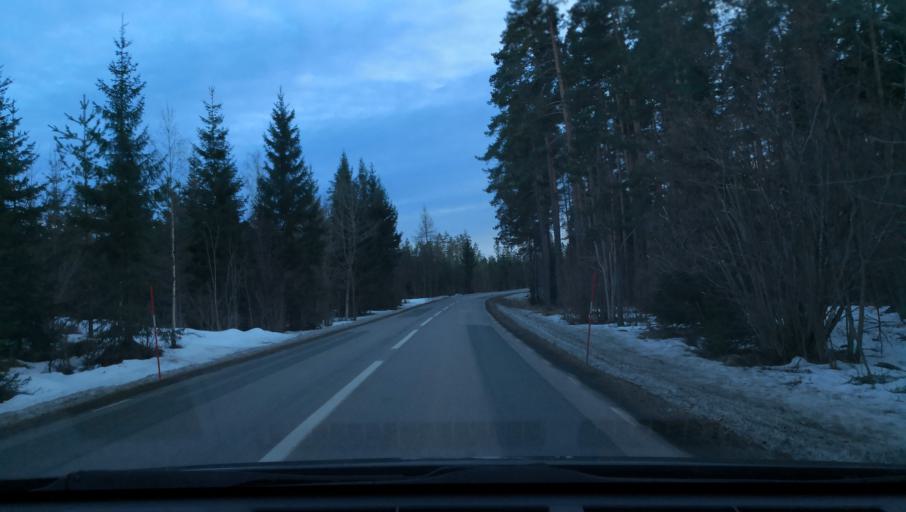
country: SE
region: Uppsala
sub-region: Osthammars Kommun
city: Osterbybruk
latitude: 60.2611
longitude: 17.9515
